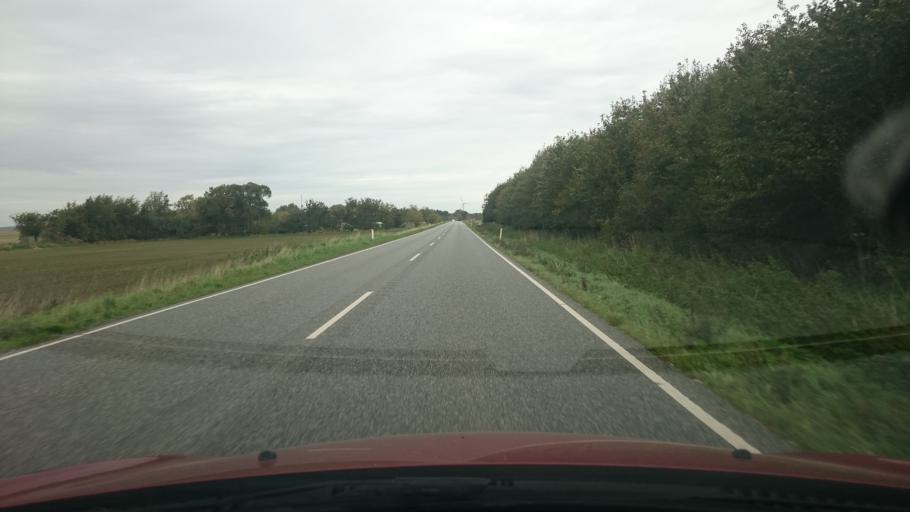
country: DK
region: North Denmark
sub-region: Mariagerfjord Kommune
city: Hadsund
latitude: 56.6028
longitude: 10.1433
